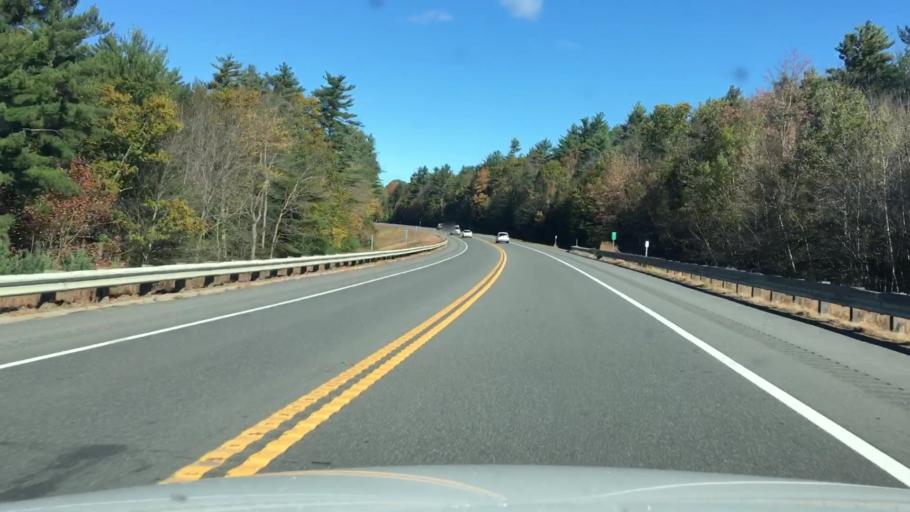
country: US
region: New Hampshire
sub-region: Strafford County
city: Farmington
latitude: 43.4529
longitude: -70.9945
